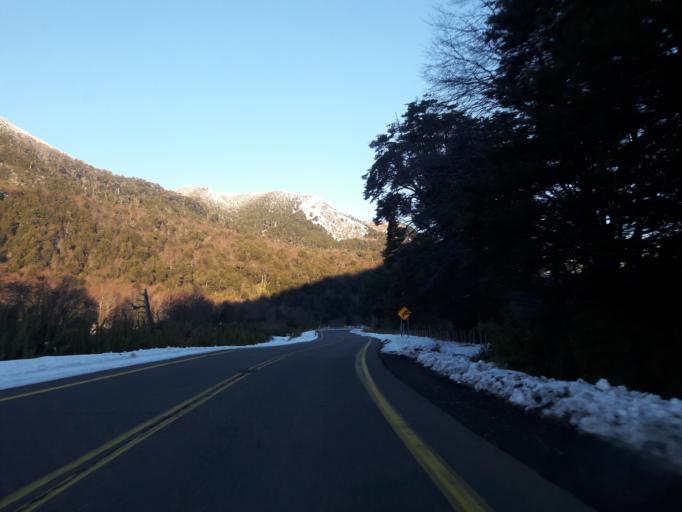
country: CL
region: Araucania
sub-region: Provincia de Cautin
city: Vilcun
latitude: -38.4913
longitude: -71.5241
